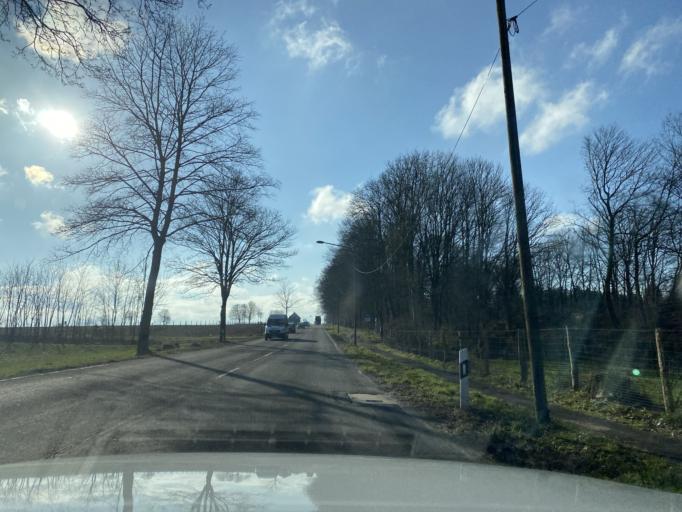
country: DE
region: North Rhine-Westphalia
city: Wermelskirchen
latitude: 51.1702
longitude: 7.2624
